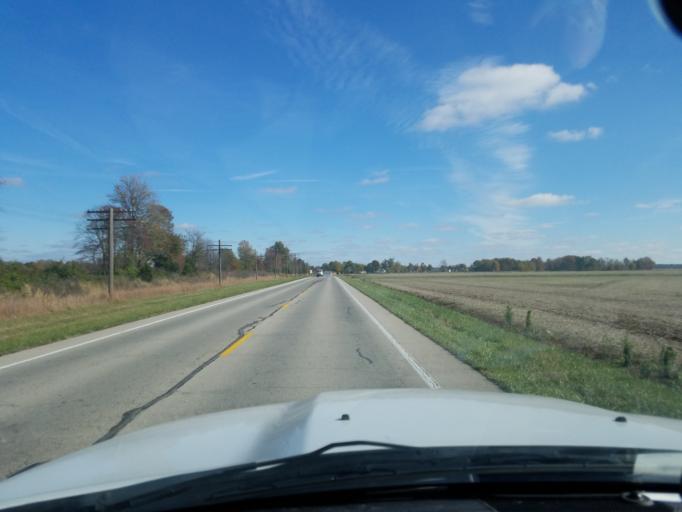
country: US
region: Indiana
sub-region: Ripley County
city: Osgood
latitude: 39.0707
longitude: -85.3978
